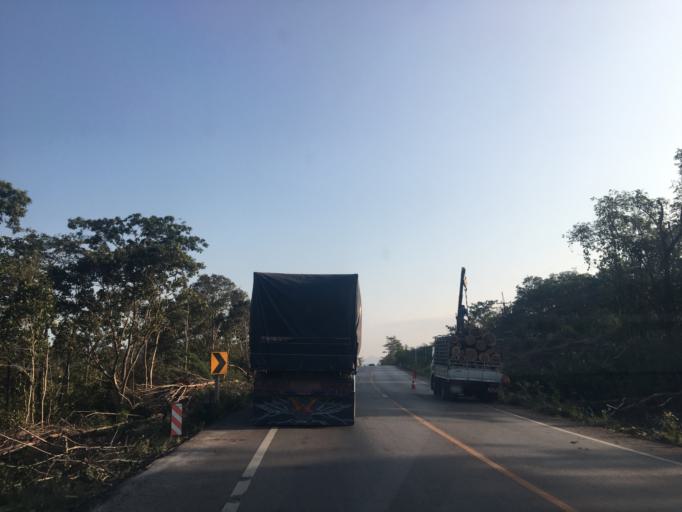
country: TH
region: Lampang
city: Ngao
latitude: 18.6616
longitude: 100.0175
